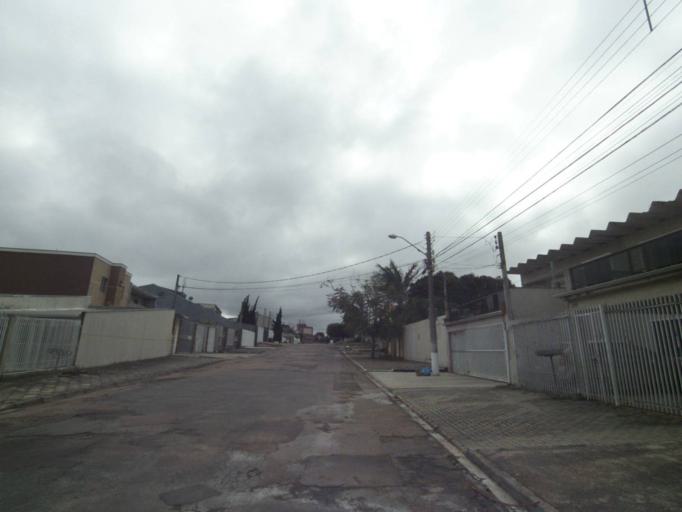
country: BR
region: Parana
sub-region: Sao Jose Dos Pinhais
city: Sao Jose dos Pinhais
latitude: -25.5228
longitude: -49.2988
